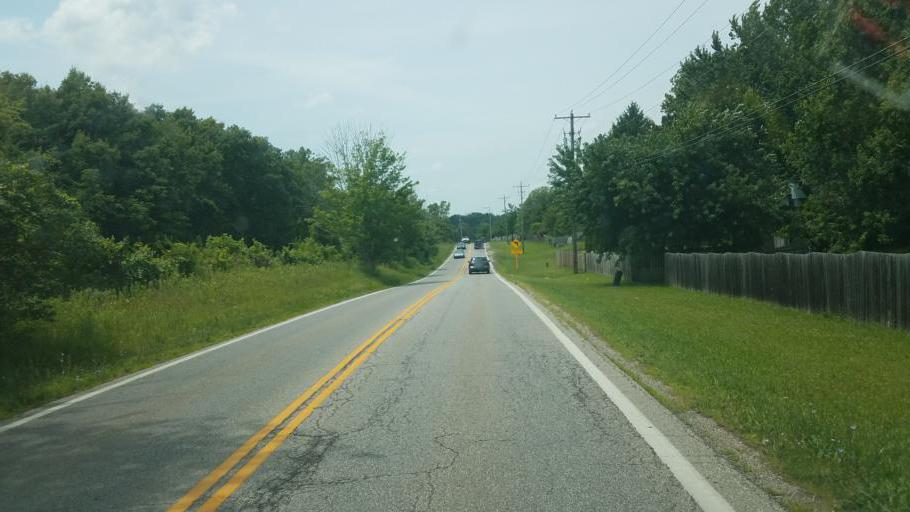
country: US
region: Ohio
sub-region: Delaware County
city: Lewis Center
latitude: 40.1572
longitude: -83.0274
